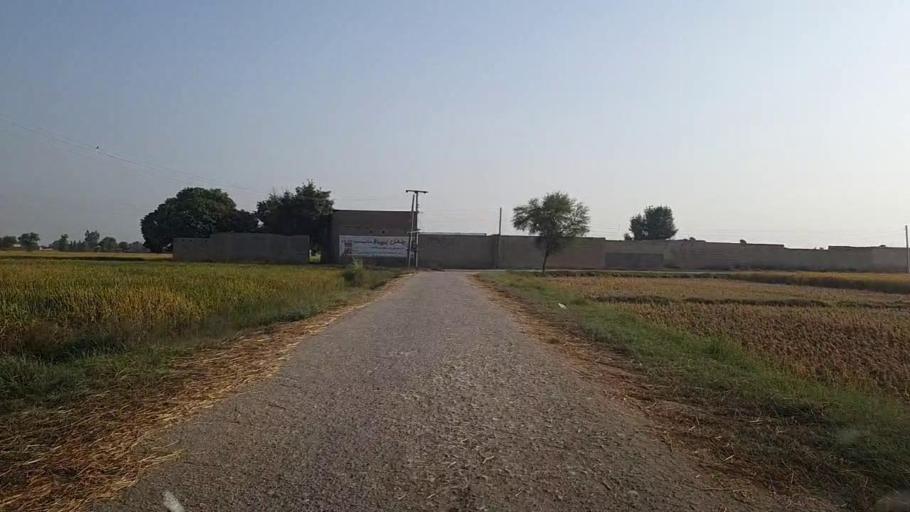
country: PK
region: Sindh
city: Kandhkot
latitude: 28.2518
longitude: 69.1602
